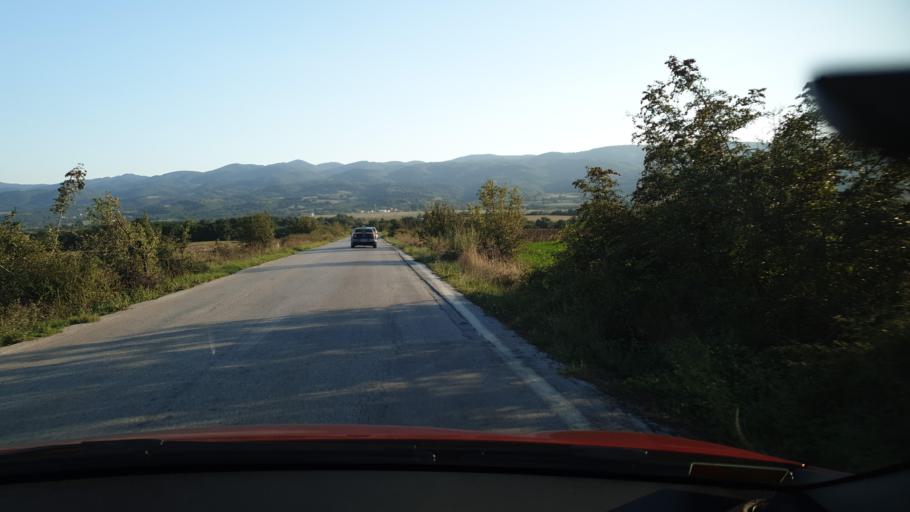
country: GR
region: Central Macedonia
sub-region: Nomos Thessalonikis
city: Gerakarou
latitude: 40.6065
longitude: 23.2239
